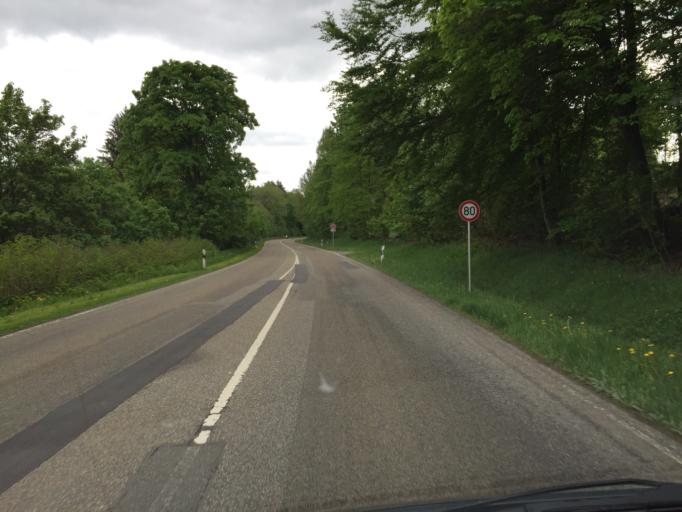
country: DE
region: Baden-Wuerttemberg
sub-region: Freiburg Region
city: Monchweiler
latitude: 48.0665
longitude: 8.4348
